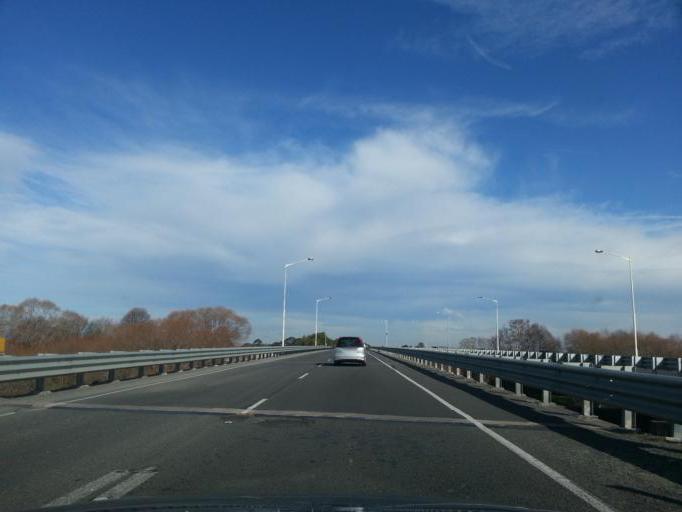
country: NZ
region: Canterbury
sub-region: Waimakariri District
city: Kaiapoi
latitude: -43.3768
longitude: 172.6457
